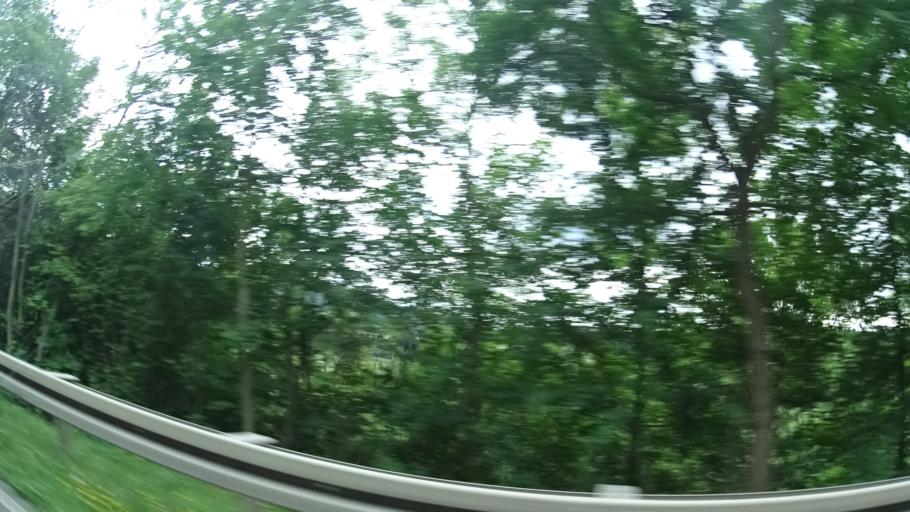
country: DE
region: Thuringia
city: Kaulsdorf
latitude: 50.6262
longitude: 11.4079
